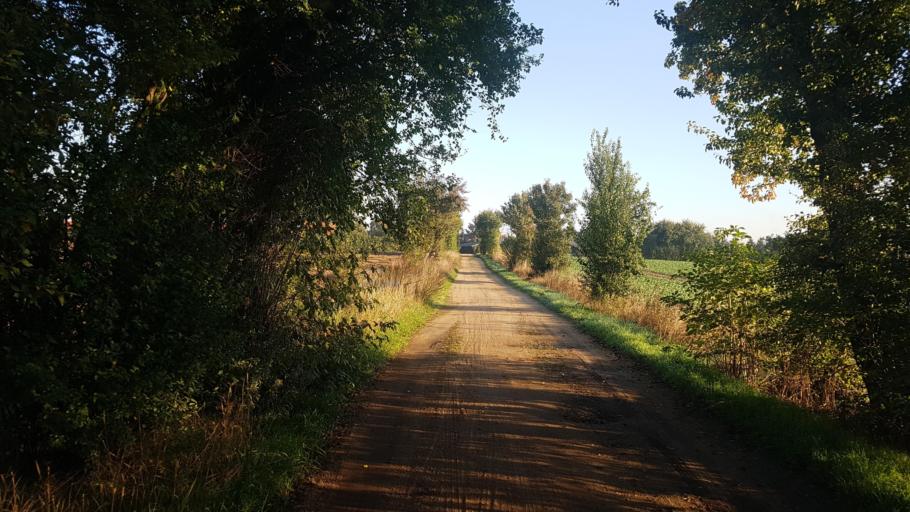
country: DE
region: Brandenburg
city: Lebusa
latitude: 51.8119
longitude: 13.4508
